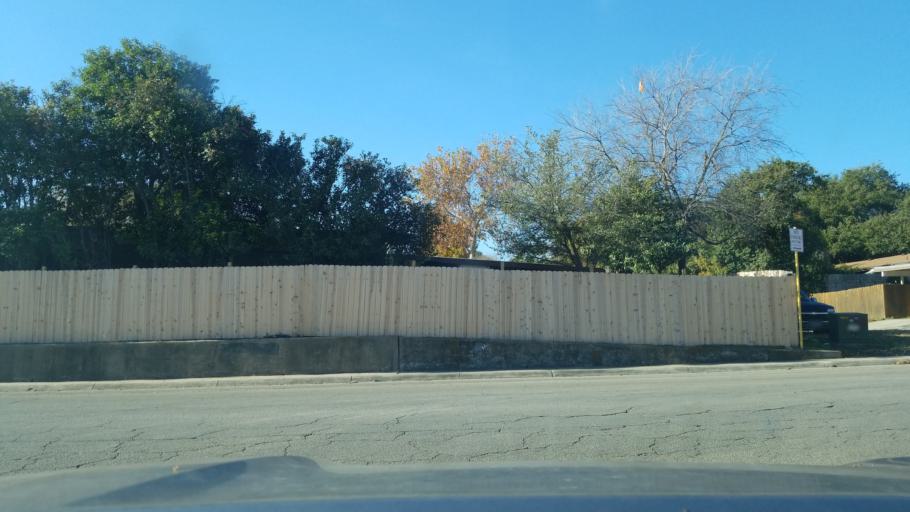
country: US
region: Texas
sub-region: Bexar County
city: Balcones Heights
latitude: 29.5310
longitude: -98.5650
